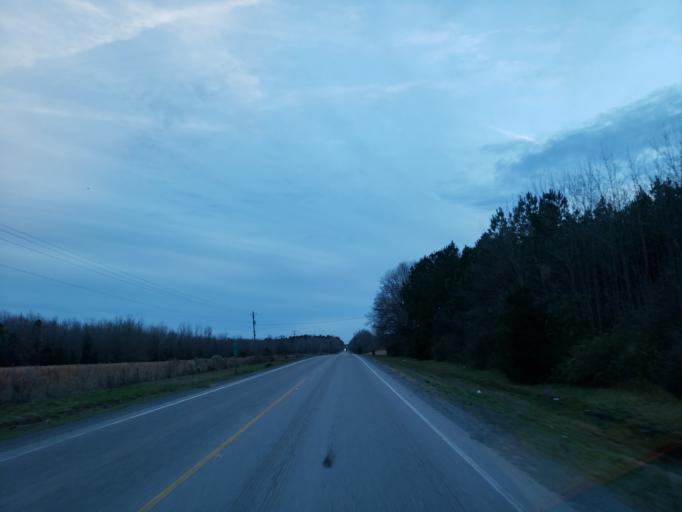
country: US
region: Alabama
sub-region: Sumter County
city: Livingston
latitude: 32.8297
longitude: -88.3095
